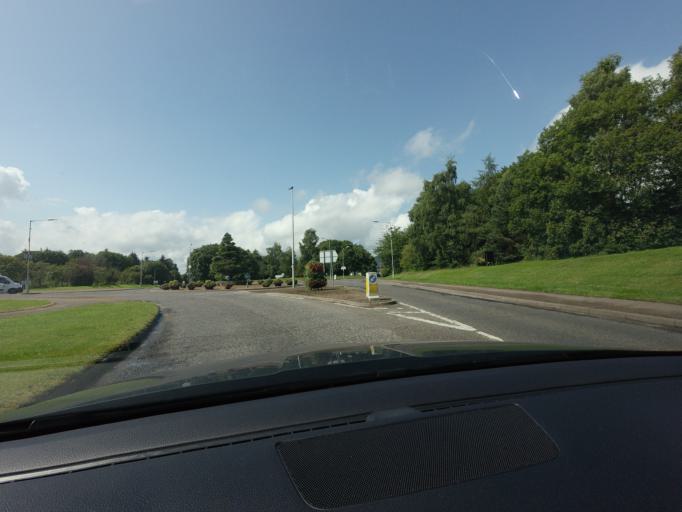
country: GB
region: Scotland
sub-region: Highland
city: Alness
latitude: 57.6928
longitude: -4.2704
